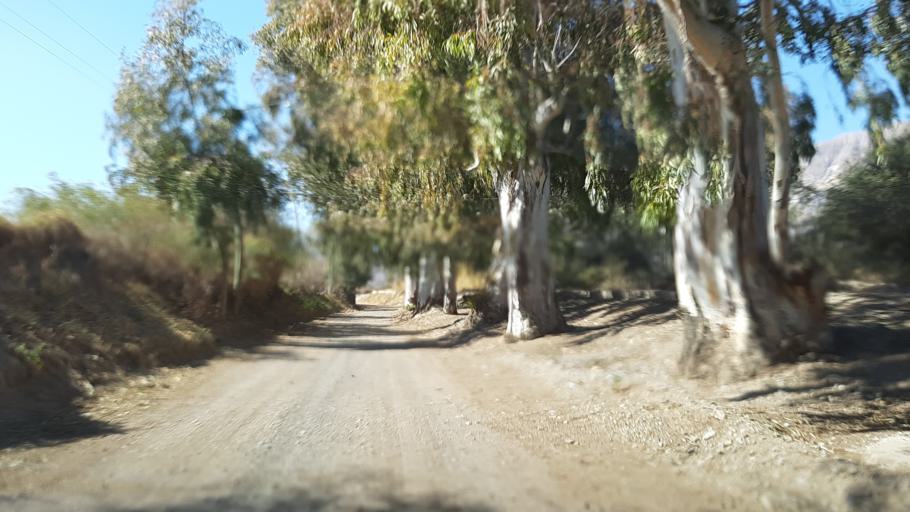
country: AR
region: San Juan
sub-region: Departamento de Zonda
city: Zonda
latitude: -31.5705
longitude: -68.7414
